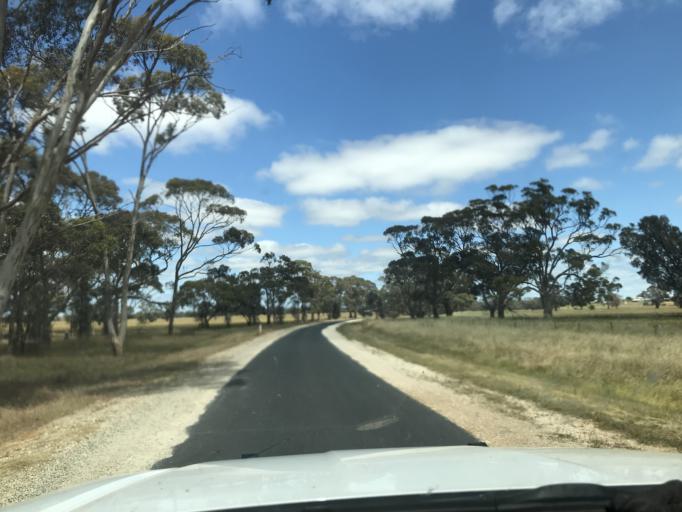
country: AU
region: South Australia
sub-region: Tatiara
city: Bordertown
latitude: -36.3082
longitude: 141.0550
